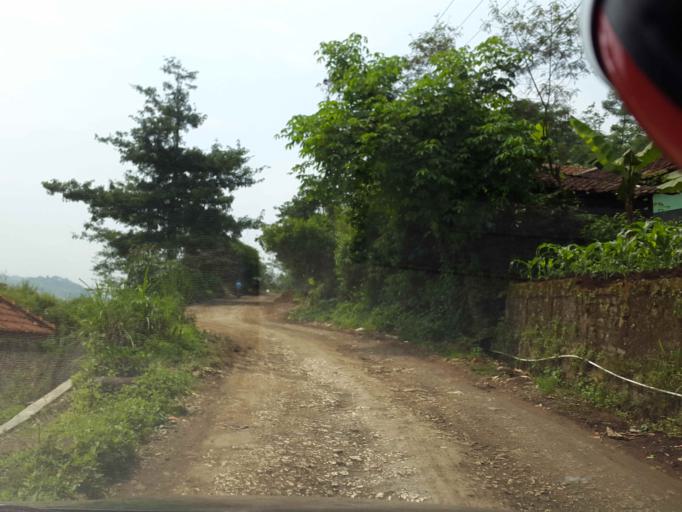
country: ID
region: West Java
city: Padalarang
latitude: -6.8578
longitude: 107.4526
